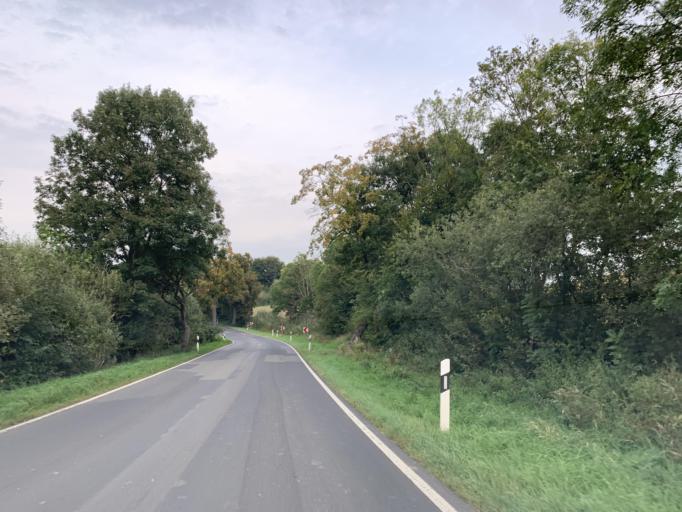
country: DE
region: Mecklenburg-Vorpommern
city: Loitz
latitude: 53.3328
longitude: 13.4968
